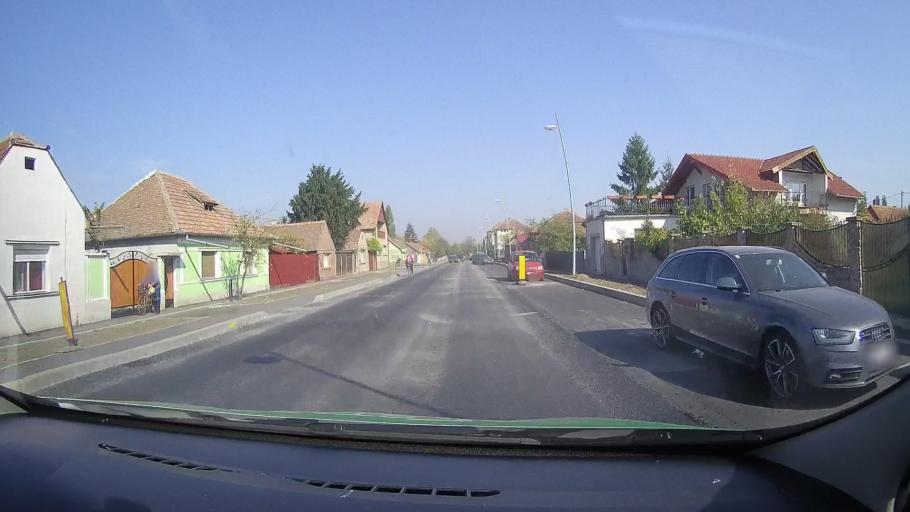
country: RO
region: Bihor
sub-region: Municipiul Salonta
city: Salonta
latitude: 46.7946
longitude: 21.6650
